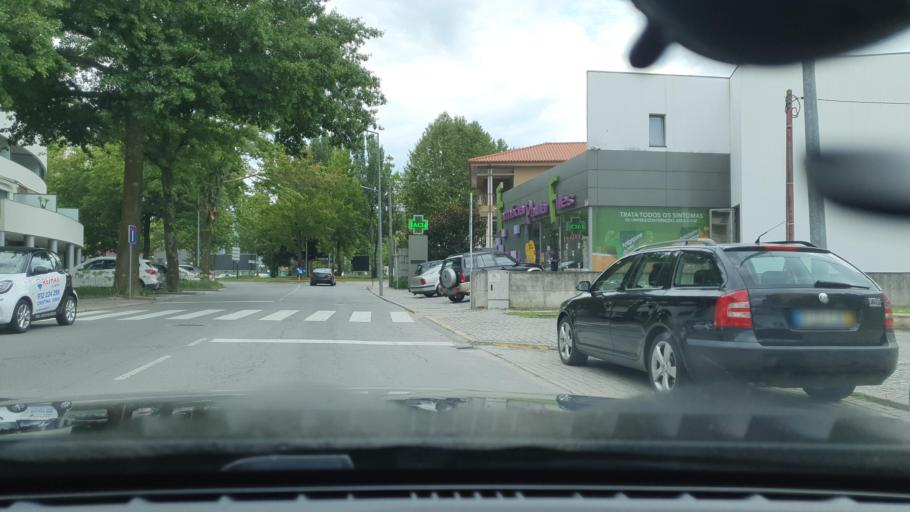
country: PT
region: Vila Real
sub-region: Chaves
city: Chaves
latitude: 41.7391
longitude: -7.4755
